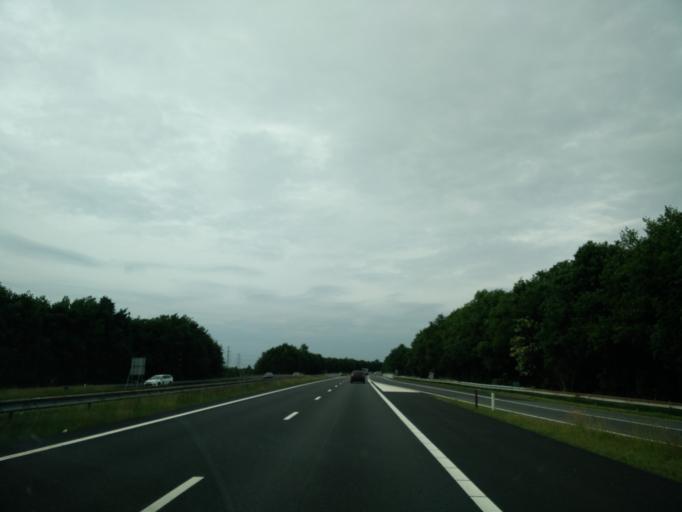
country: NL
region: Drenthe
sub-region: Gemeente Assen
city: Assen
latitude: 52.9958
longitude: 6.5258
